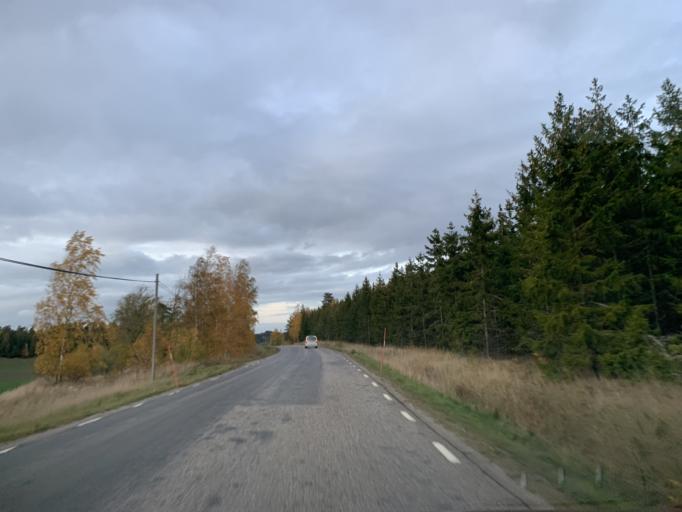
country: SE
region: Stockholm
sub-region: Nynashamns Kommun
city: Osmo
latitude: 58.9454
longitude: 17.7619
